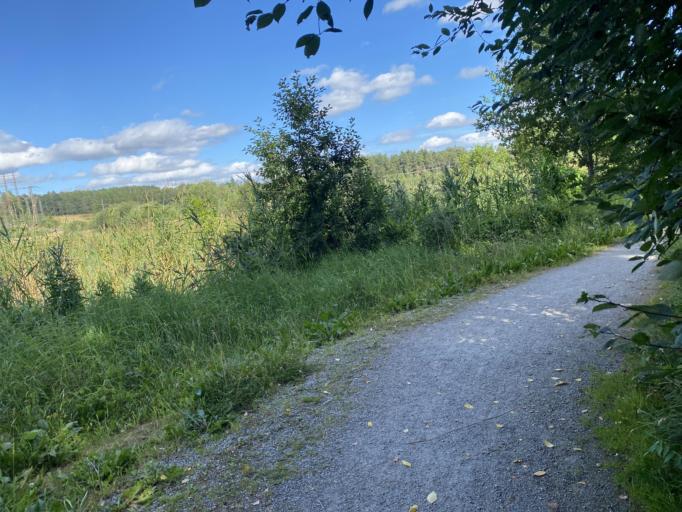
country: SE
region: Stockholm
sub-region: Upplands Vasby Kommun
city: Upplands Vaesby
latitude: 59.4865
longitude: 17.8993
